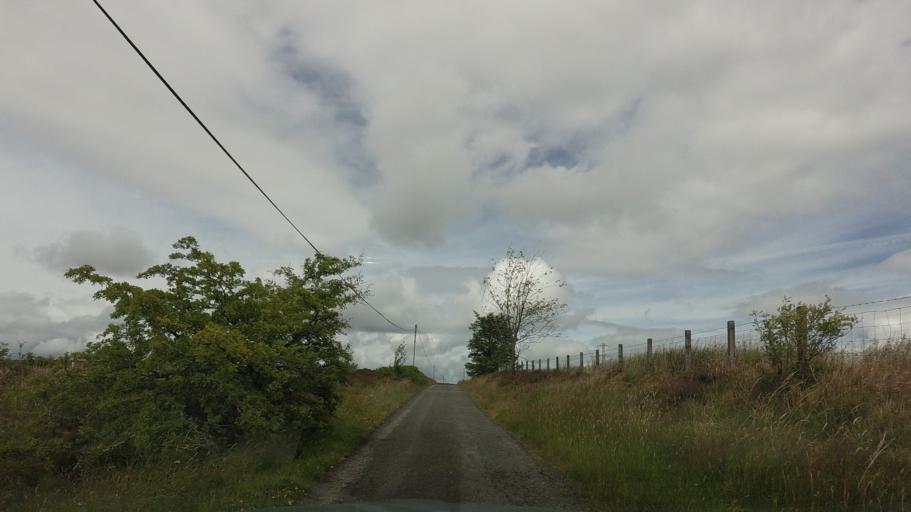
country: GB
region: Scotland
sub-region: Stirling
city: Killearn
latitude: 56.0939
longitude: -4.4319
